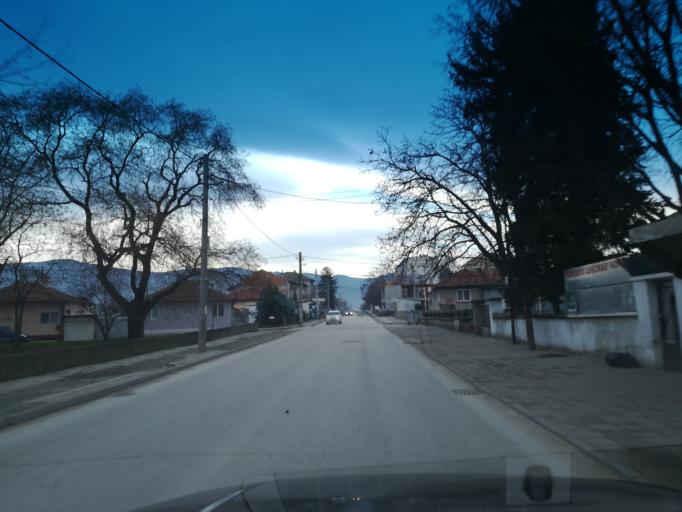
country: BG
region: Plovdiv
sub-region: Obshtina Plovdiv
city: Plovdiv
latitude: 42.1000
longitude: 24.7017
